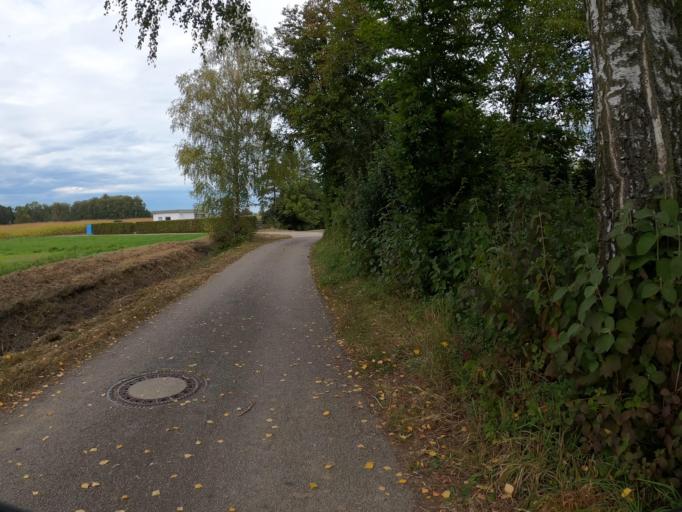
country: DE
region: Bavaria
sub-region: Swabia
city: Holzheim
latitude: 48.3885
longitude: 10.0761
